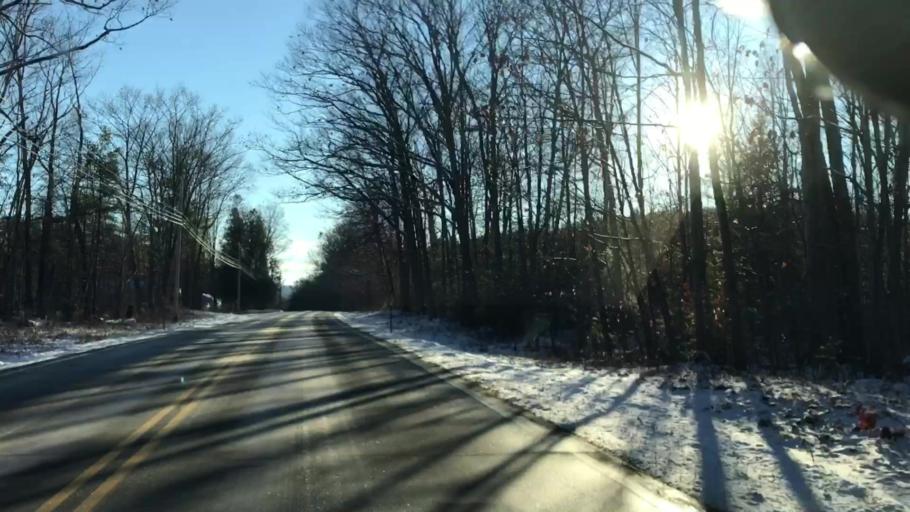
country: US
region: New Hampshire
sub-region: Grafton County
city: Haverhill
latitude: 43.9894
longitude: -72.0788
